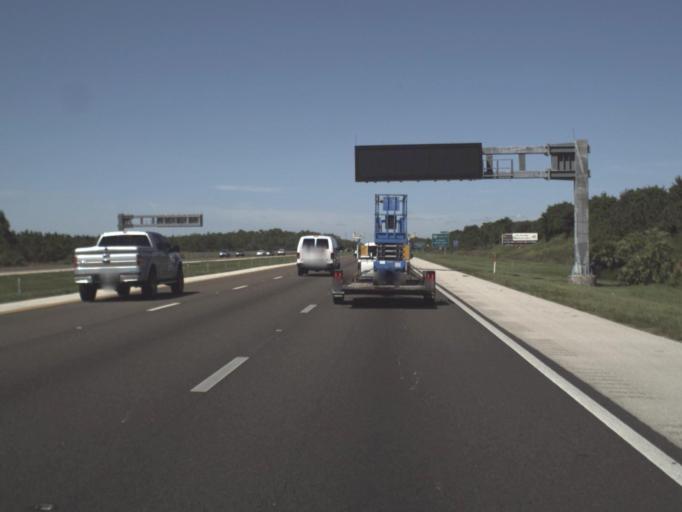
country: US
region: Florida
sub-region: Lee County
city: Gateway
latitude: 26.5885
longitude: -81.7959
